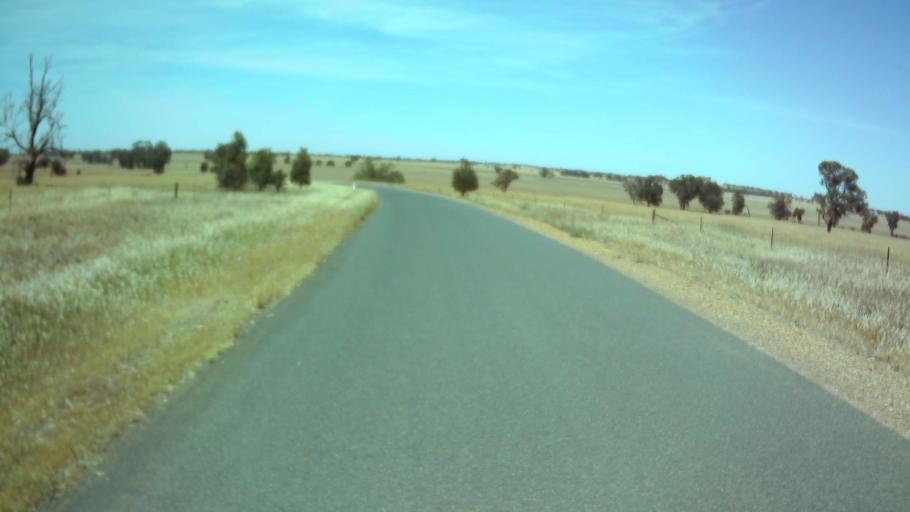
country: AU
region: New South Wales
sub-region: Weddin
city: Grenfell
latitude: -33.8574
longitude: 147.9298
